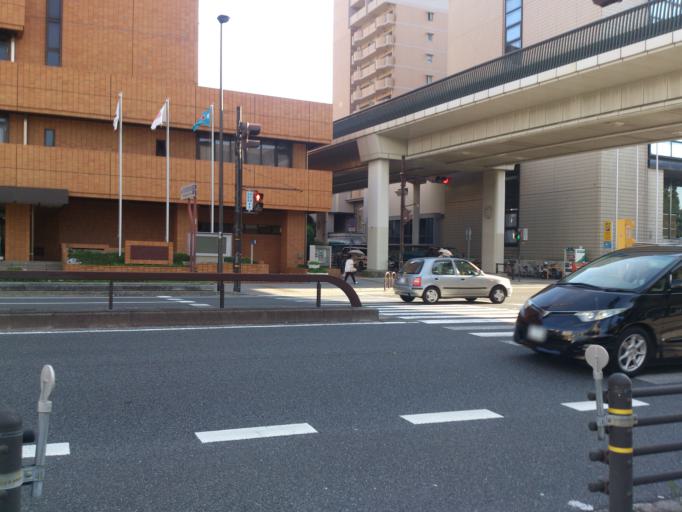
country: JP
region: Hyogo
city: Amagasaki
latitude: 34.7203
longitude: 135.4205
